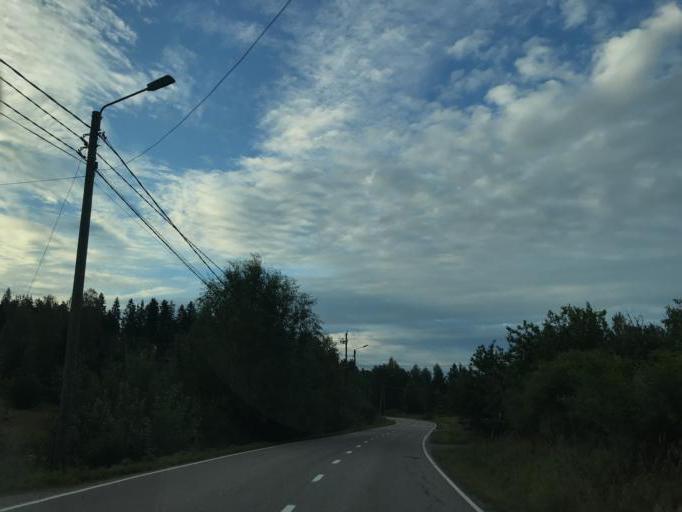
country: FI
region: Uusimaa
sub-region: Helsinki
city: Vihti
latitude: 60.3953
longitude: 24.5117
